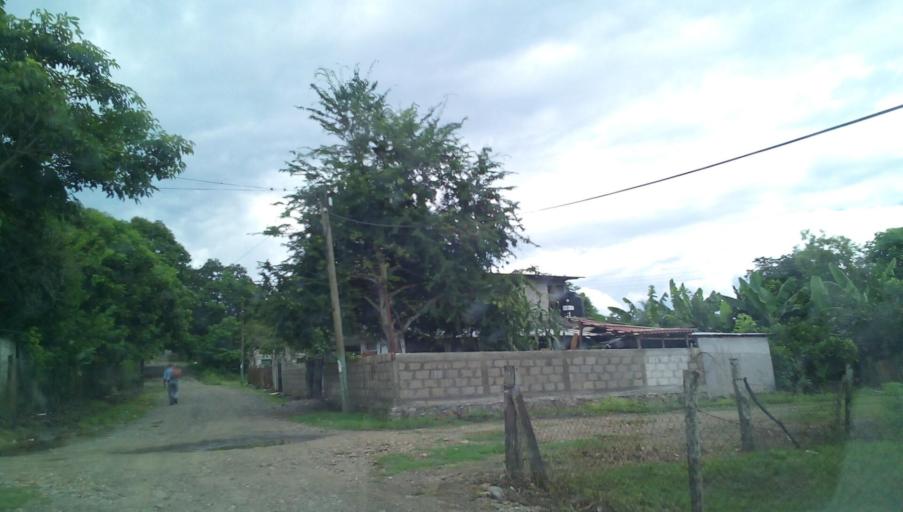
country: MX
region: Veracruz
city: Tepetzintla
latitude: 21.1266
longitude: -97.8560
